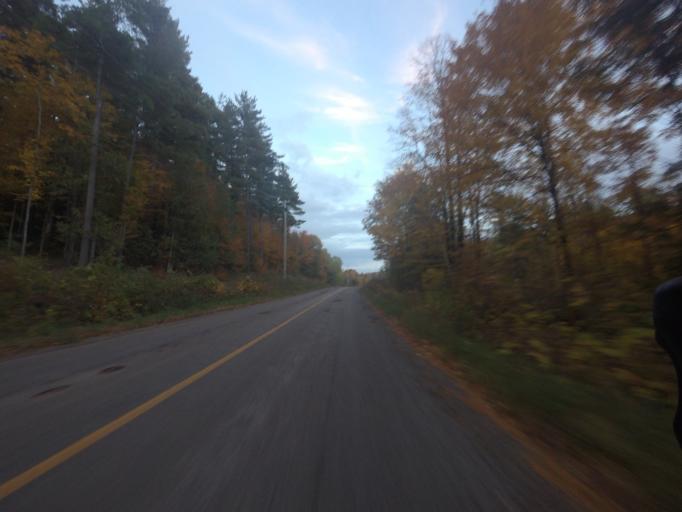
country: CA
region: Ontario
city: Renfrew
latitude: 45.3542
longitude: -76.9527
